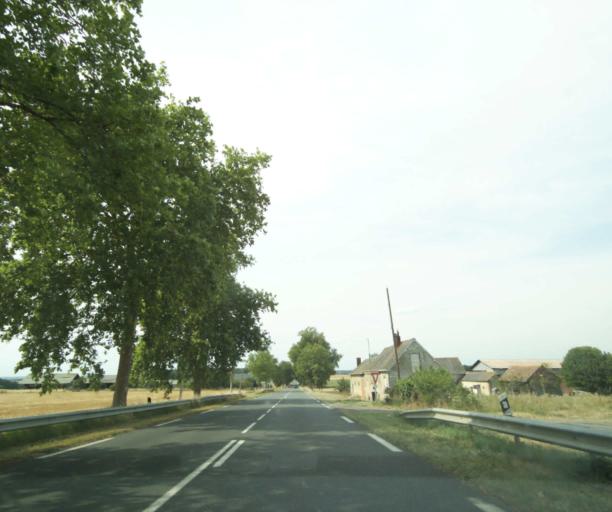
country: FR
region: Centre
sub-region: Departement d'Indre-et-Loire
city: Saint-Christophe-sur-le-Nais
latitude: 47.6373
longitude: 0.5004
